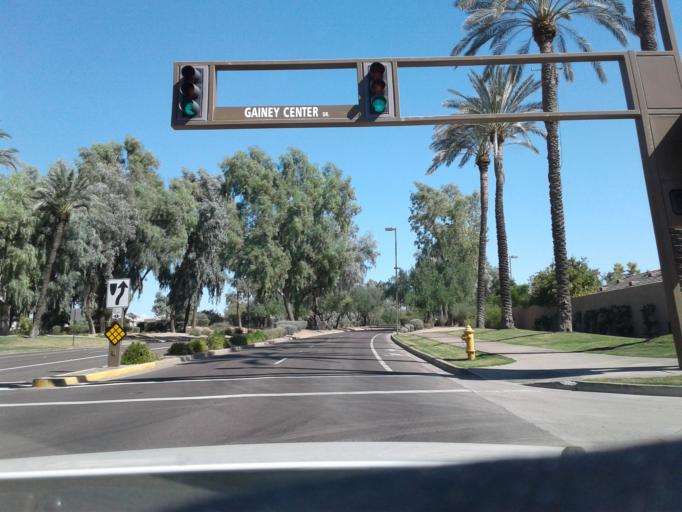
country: US
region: Arizona
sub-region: Maricopa County
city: Paradise Valley
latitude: 33.5640
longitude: -111.9135
